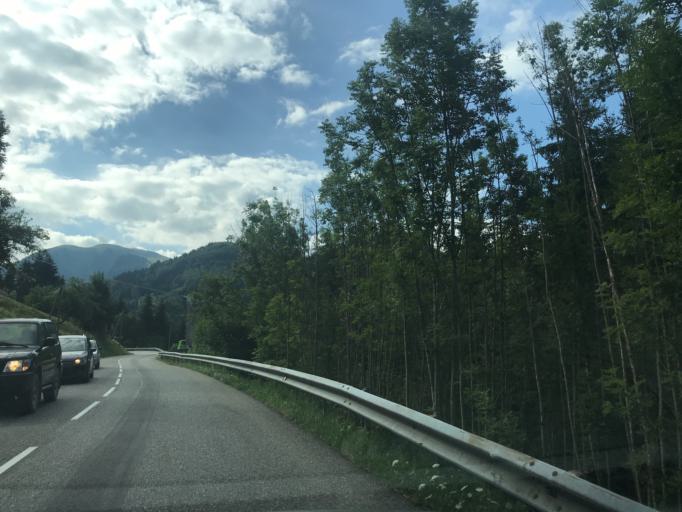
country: FR
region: Rhone-Alpes
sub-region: Departement de la Haute-Savoie
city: Thones
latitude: 45.8618
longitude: 6.3307
